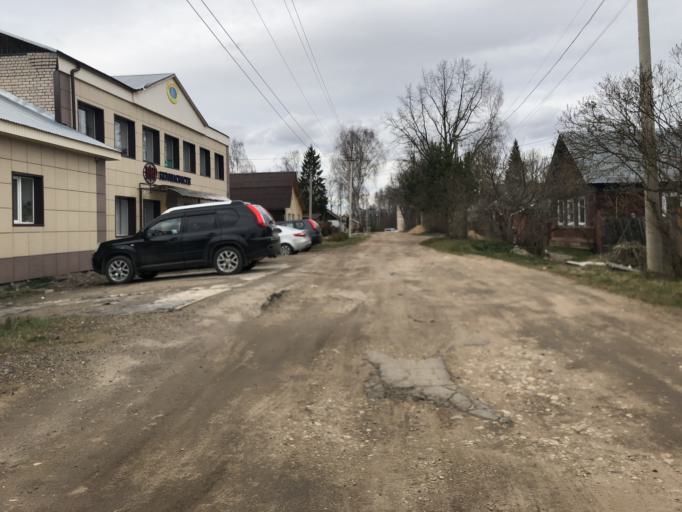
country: RU
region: Tverskaya
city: Rzhev
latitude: 56.2542
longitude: 34.3174
